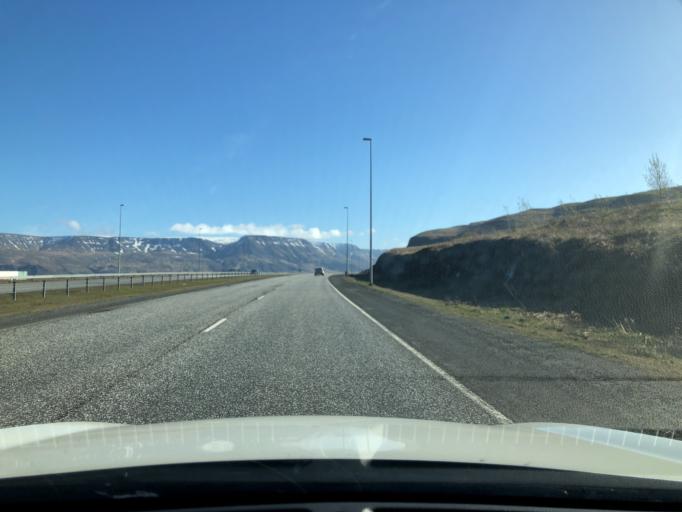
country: IS
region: Capital Region
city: Mosfellsbaer
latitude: 64.1439
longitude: -21.7541
